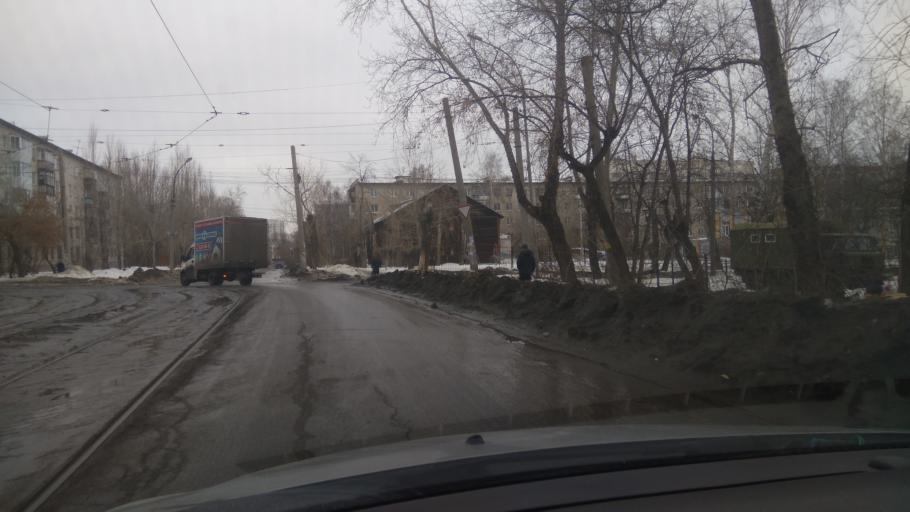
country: RU
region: Sverdlovsk
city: Yekaterinburg
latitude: 56.8971
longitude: 60.6361
